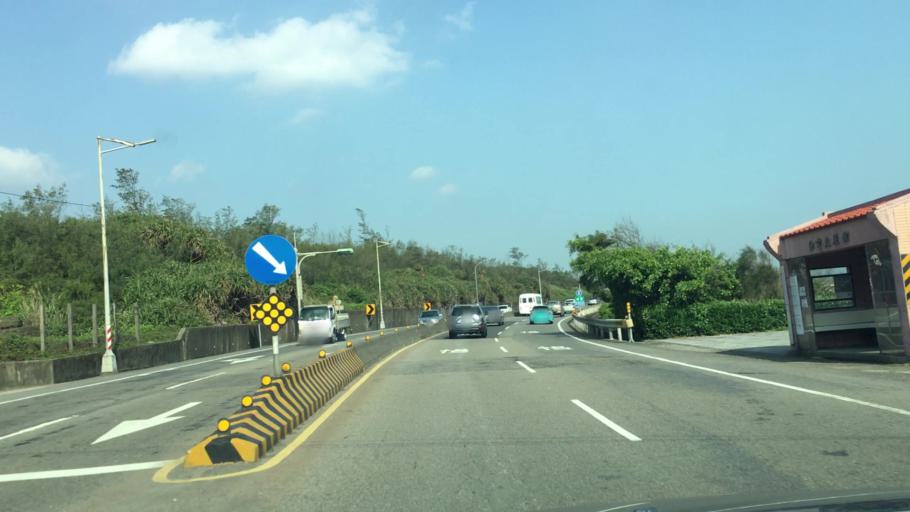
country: TW
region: Taiwan
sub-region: Keelung
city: Keelung
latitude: 25.2072
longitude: 121.6599
